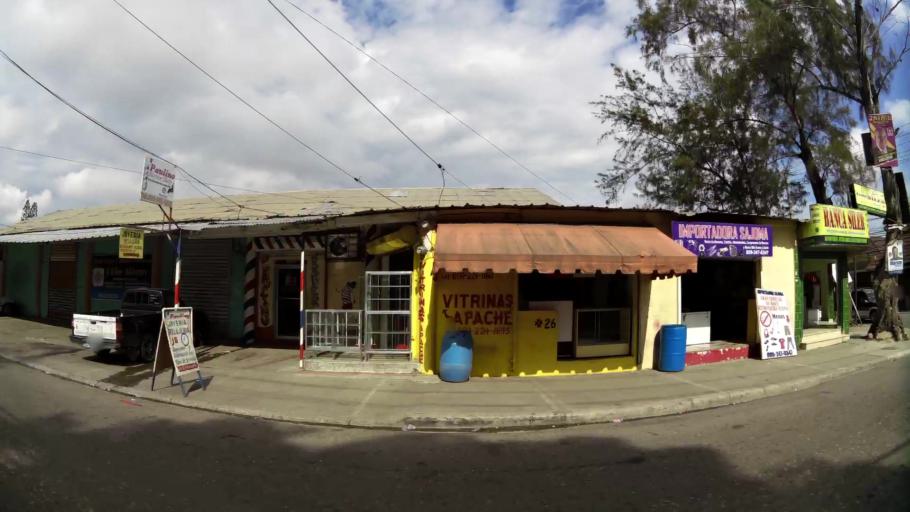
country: DO
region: Santiago
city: Santiago de los Caballeros
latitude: 19.4438
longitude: -70.7070
